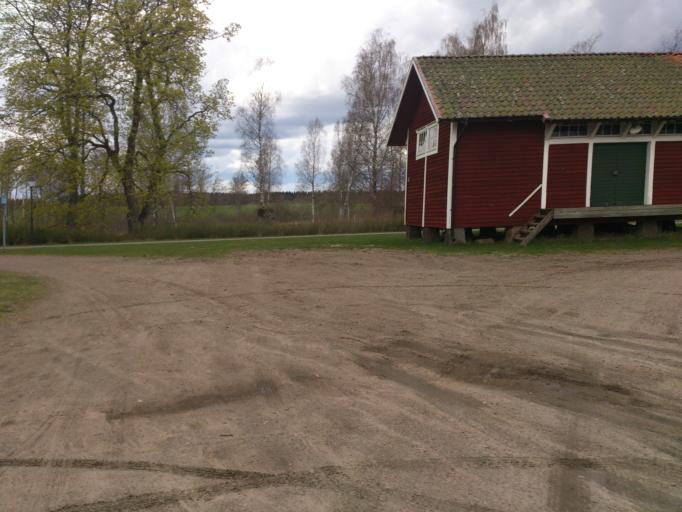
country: SE
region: Vaestra Goetaland
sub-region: Falkopings Kommun
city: Falkoeping
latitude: 57.9874
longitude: 13.5329
